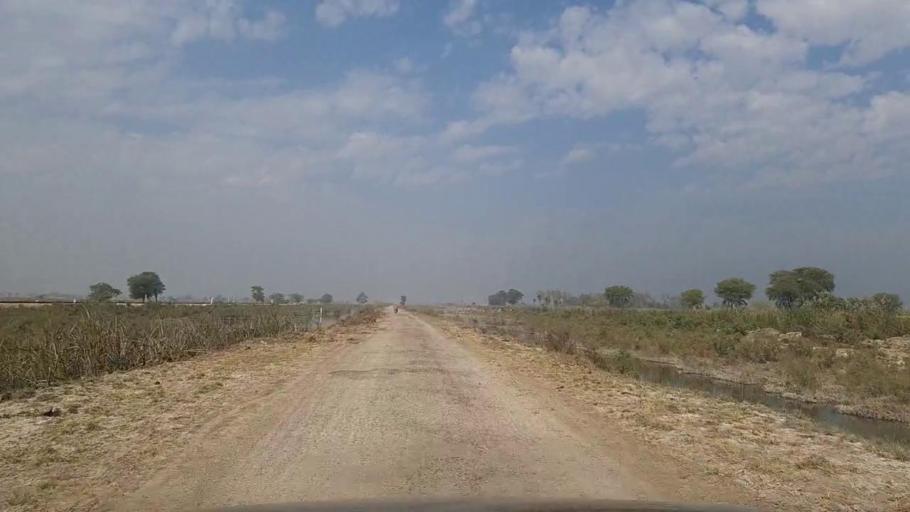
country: PK
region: Sindh
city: Daur
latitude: 26.3938
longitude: 68.3490
